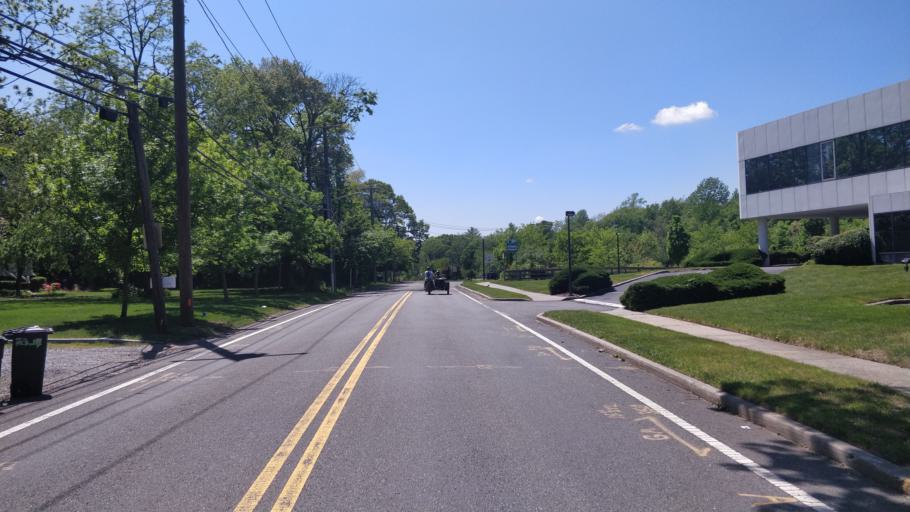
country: US
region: New York
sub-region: Suffolk County
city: Hauppauge
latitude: 40.8253
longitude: -73.2068
